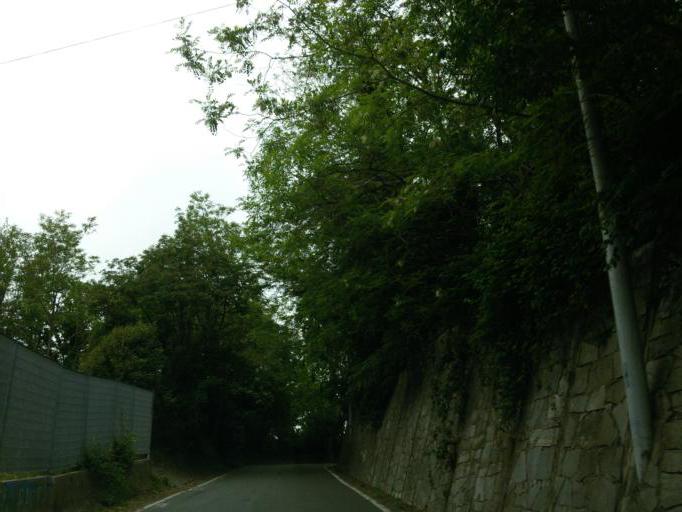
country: IT
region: Liguria
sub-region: Provincia di Genova
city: Genoa
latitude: 44.4306
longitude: 8.9105
